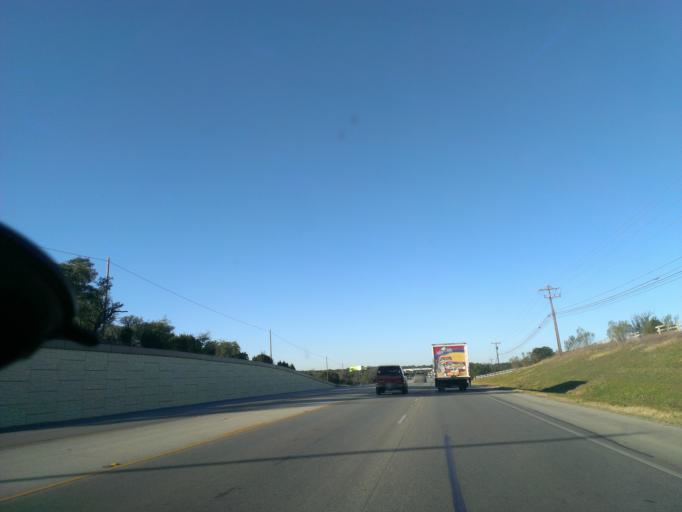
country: US
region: Texas
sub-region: Hays County
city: Dripping Springs
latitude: 30.1998
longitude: -97.9911
